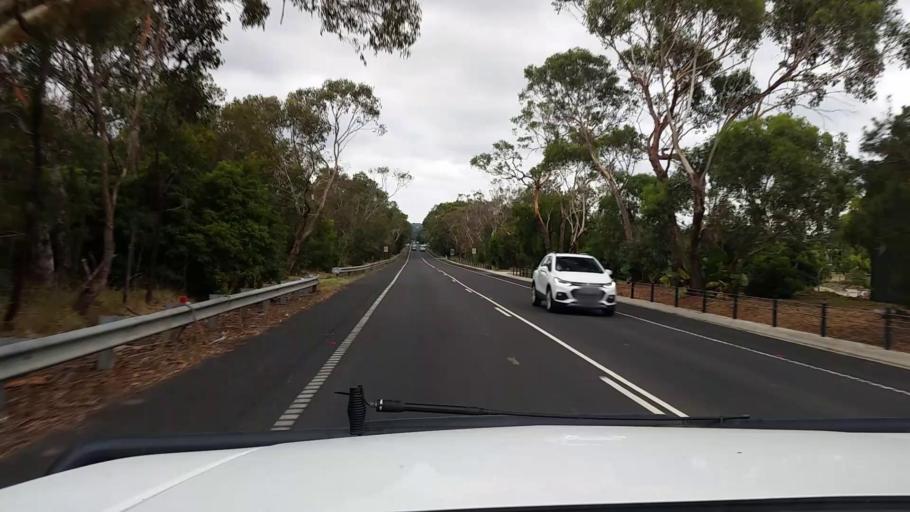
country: AU
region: Victoria
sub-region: Mornington Peninsula
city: Somerville
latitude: -38.2172
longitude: 145.1710
